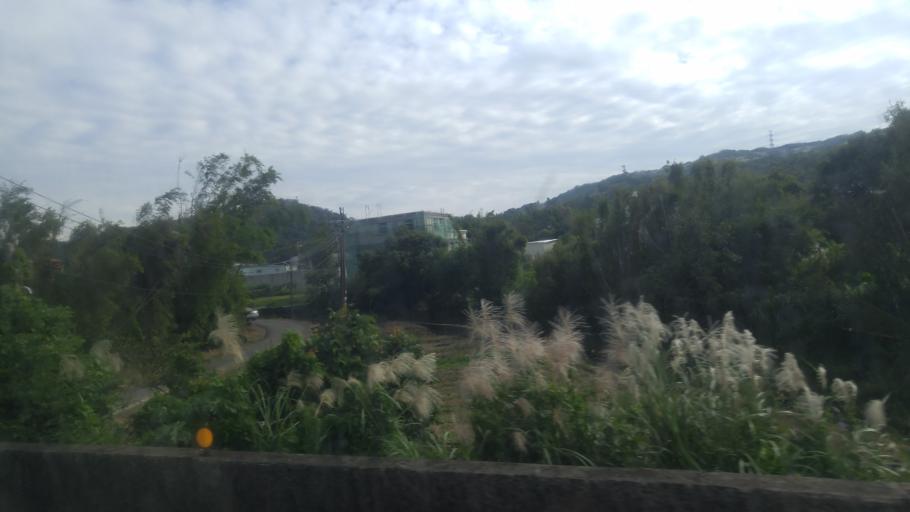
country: TW
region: Taiwan
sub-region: Hsinchu
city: Zhubei
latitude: 24.8929
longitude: 121.1196
